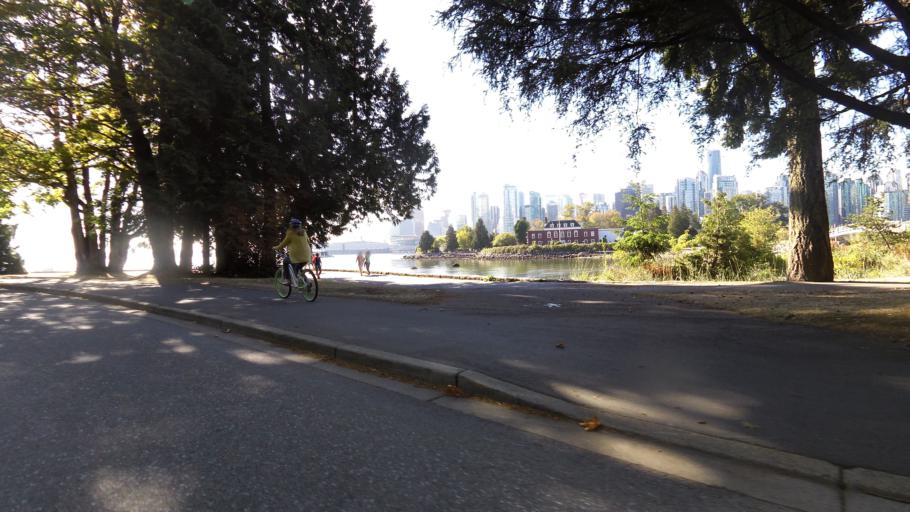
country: CA
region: British Columbia
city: West End
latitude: 49.2979
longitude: -123.1235
